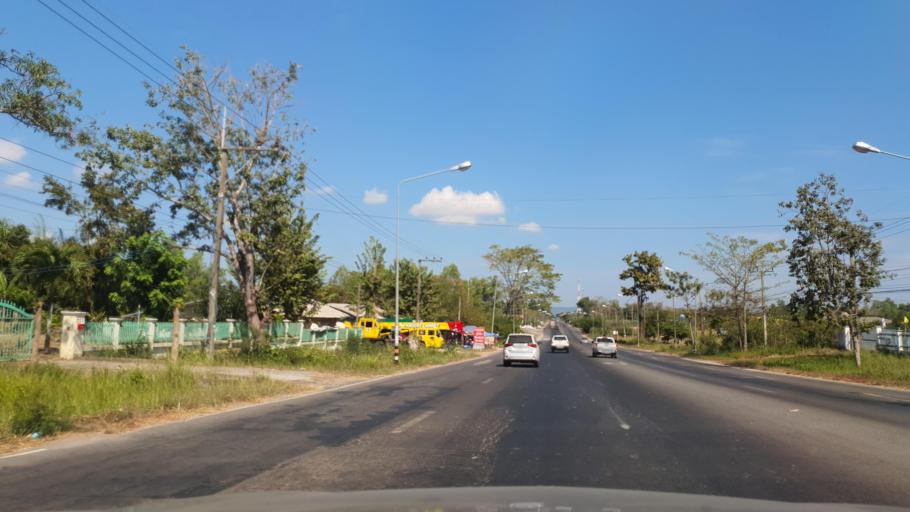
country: TH
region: Kalasin
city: Somdet
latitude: 16.7151
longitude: 103.7548
